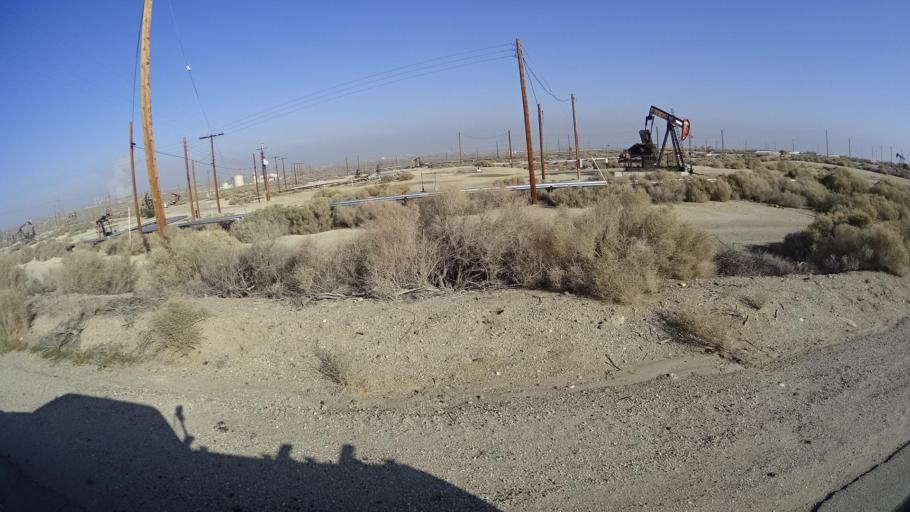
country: US
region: California
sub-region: Kern County
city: Taft Heights
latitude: 35.1889
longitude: -119.5698
